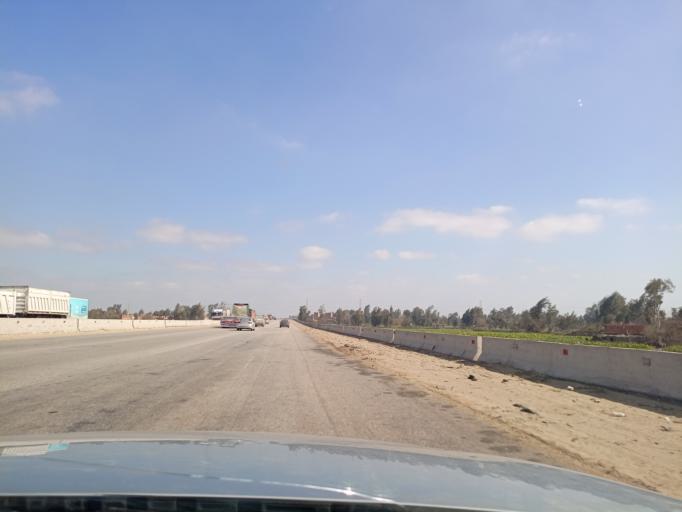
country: EG
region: Muhafazat al Minufiyah
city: Al Bajur
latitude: 30.4330
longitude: 31.1023
